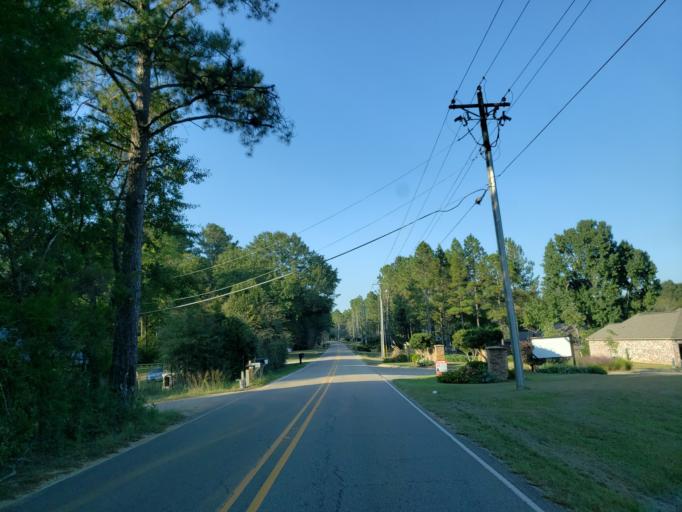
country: US
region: Mississippi
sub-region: Lamar County
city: West Hattiesburg
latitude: 31.2988
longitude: -89.4463
